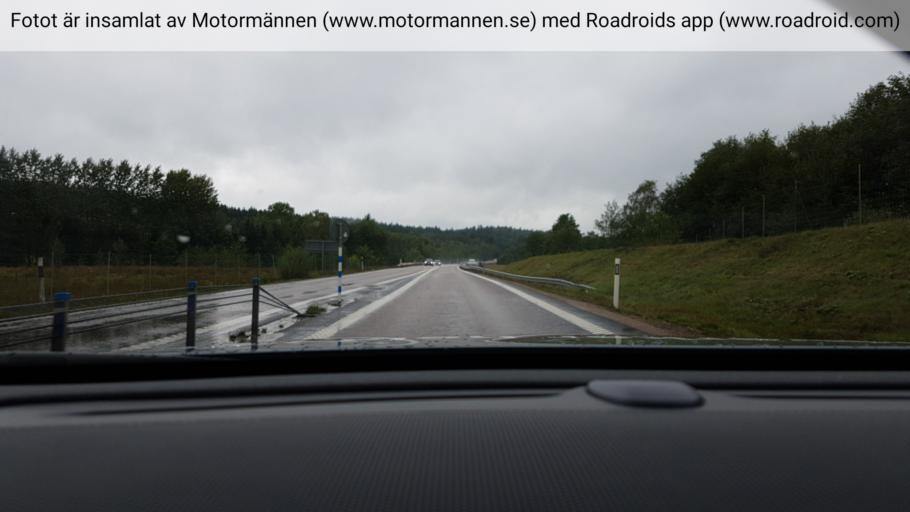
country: SE
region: Vaestra Goetaland
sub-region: Uddevalla Kommun
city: Uddevalla
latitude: 58.3320
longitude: 11.9757
